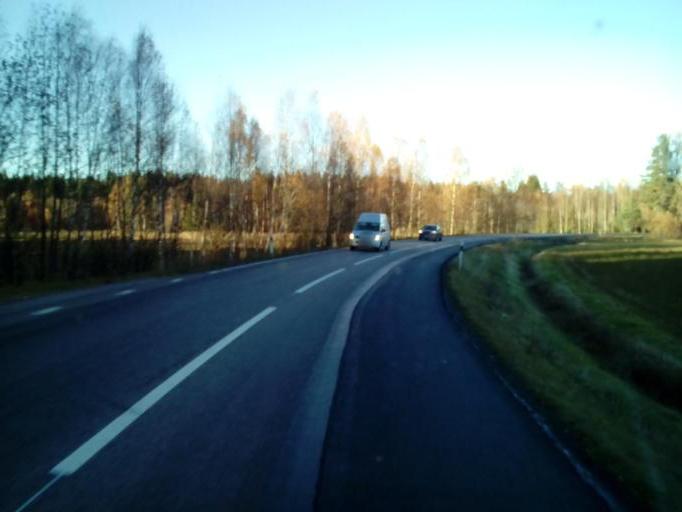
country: SE
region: OErebro
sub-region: Hallsbergs Kommun
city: Palsboda
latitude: 58.8284
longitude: 15.4068
